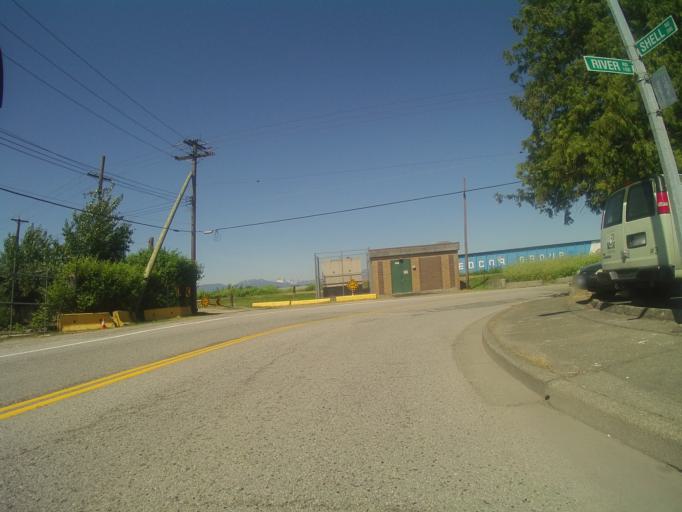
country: CA
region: British Columbia
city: Richmond
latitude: 49.1976
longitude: -123.1027
